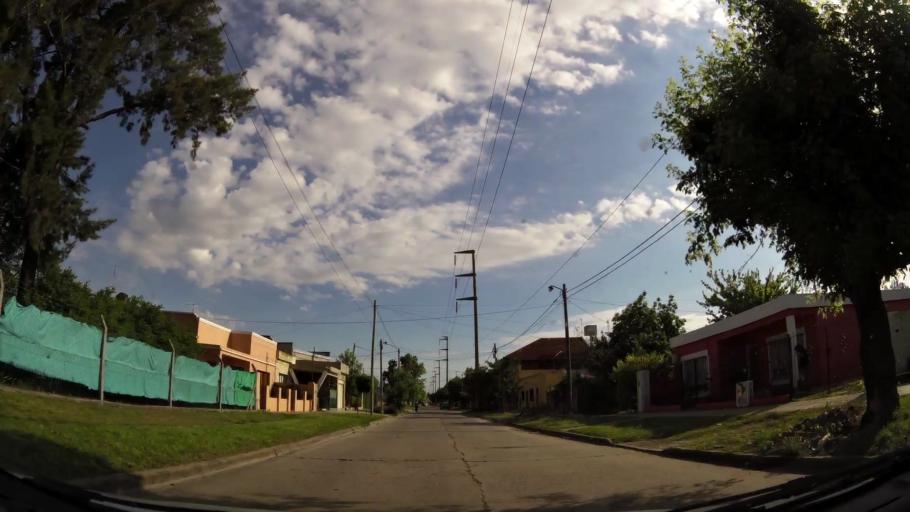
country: AR
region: Buenos Aires
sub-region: Partido de Merlo
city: Merlo
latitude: -34.6590
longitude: -58.7341
